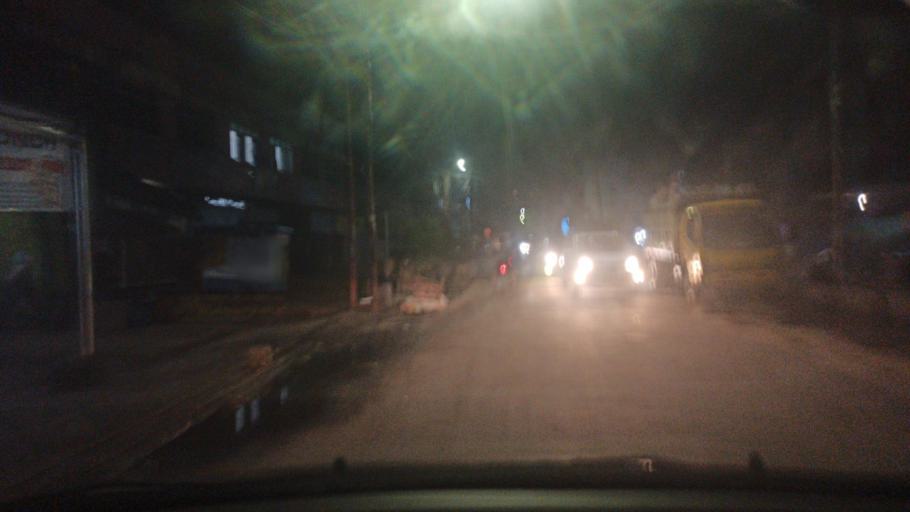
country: ID
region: South Sumatra
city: Palembang
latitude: -2.9301
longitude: 104.7892
